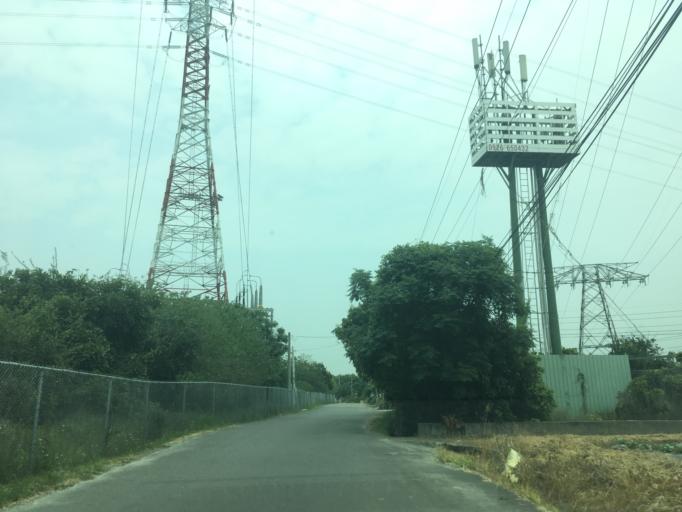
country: TW
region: Taiwan
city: Zhongxing New Village
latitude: 24.0456
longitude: 120.6798
